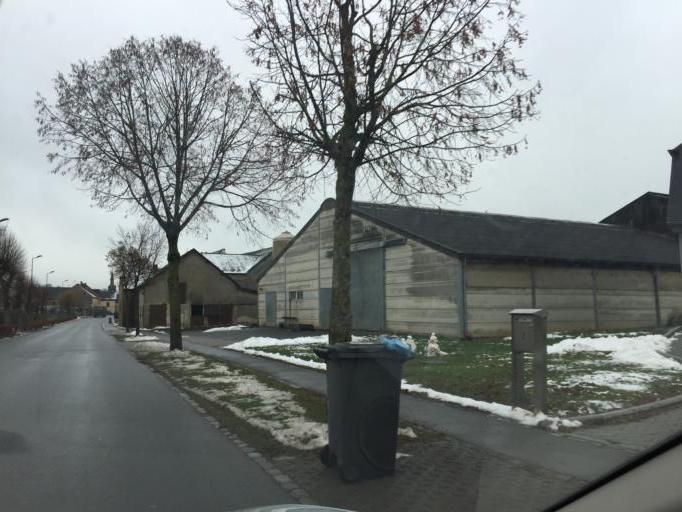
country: LU
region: Diekirch
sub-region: Canton de Diekirch
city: Mertzig
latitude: 49.8360
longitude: 6.0109
